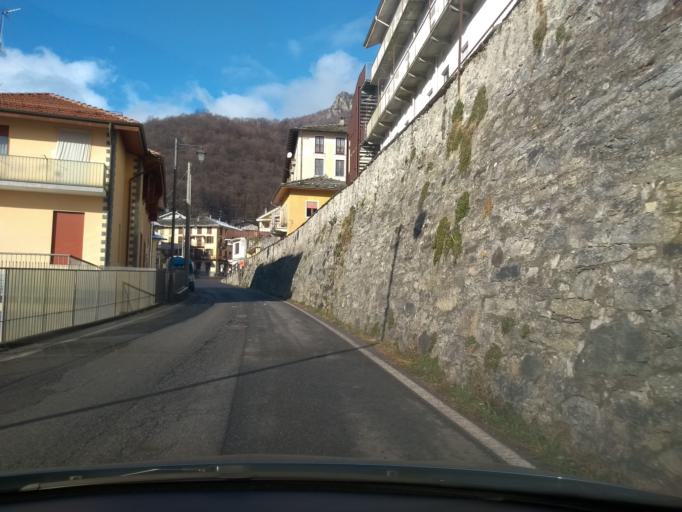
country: IT
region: Piedmont
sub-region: Provincia di Torino
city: Ceres
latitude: 45.3125
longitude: 7.3900
